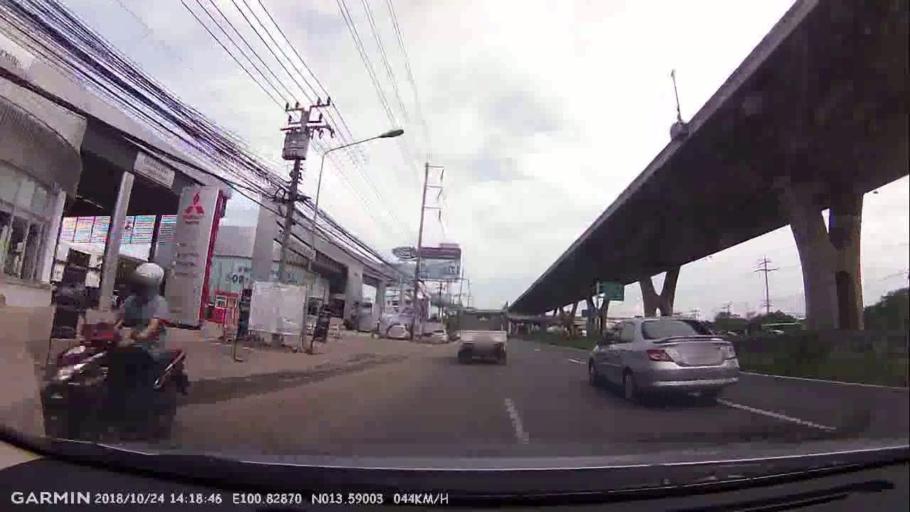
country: TH
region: Samut Prakan
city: Bang Sao Thong
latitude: 13.5900
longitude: 100.8288
